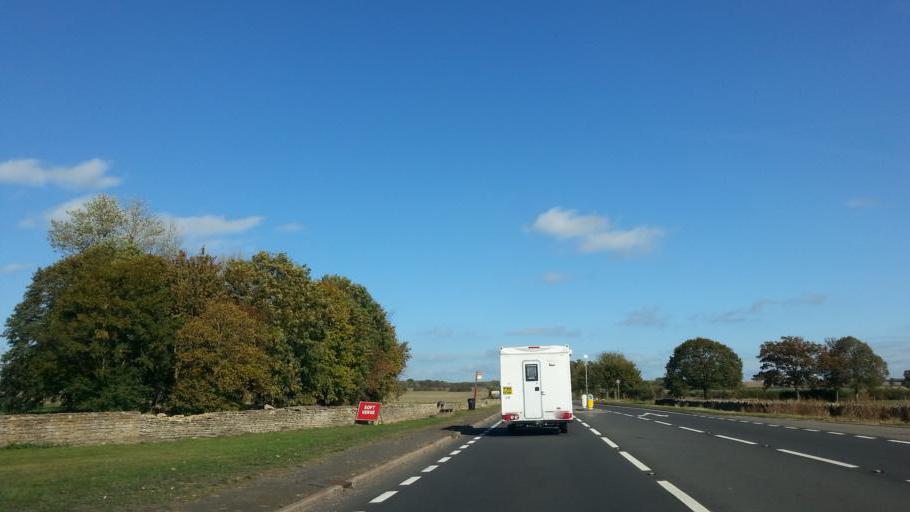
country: GB
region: England
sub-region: Northamptonshire
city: Thrapston
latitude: 52.4221
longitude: -0.4946
